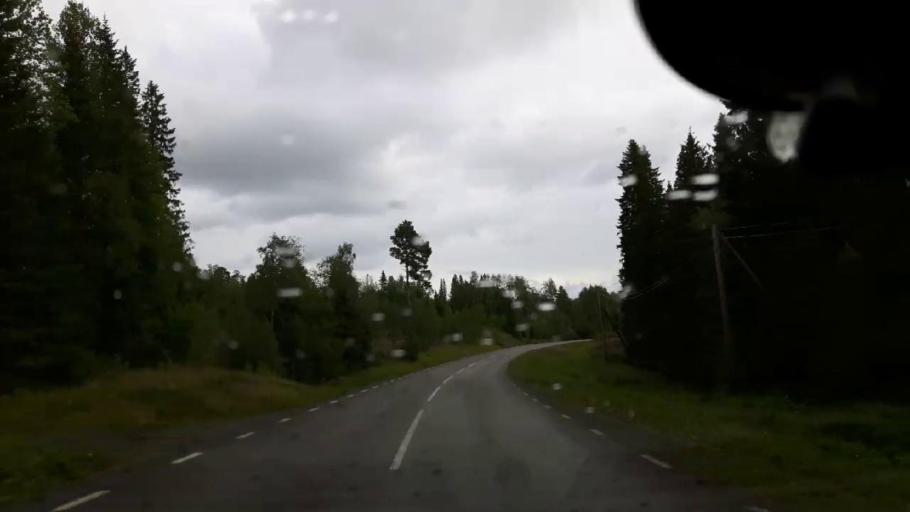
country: SE
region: Jaemtland
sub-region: Krokoms Kommun
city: Valla
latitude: 63.4149
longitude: 13.8026
